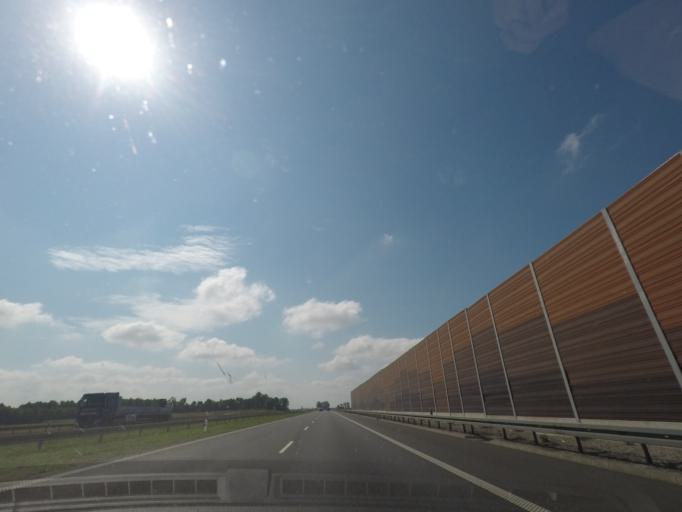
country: PL
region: Kujawsko-Pomorskie
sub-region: Powiat aleksandrowski
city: Waganiec
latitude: 52.7830
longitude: 18.8426
